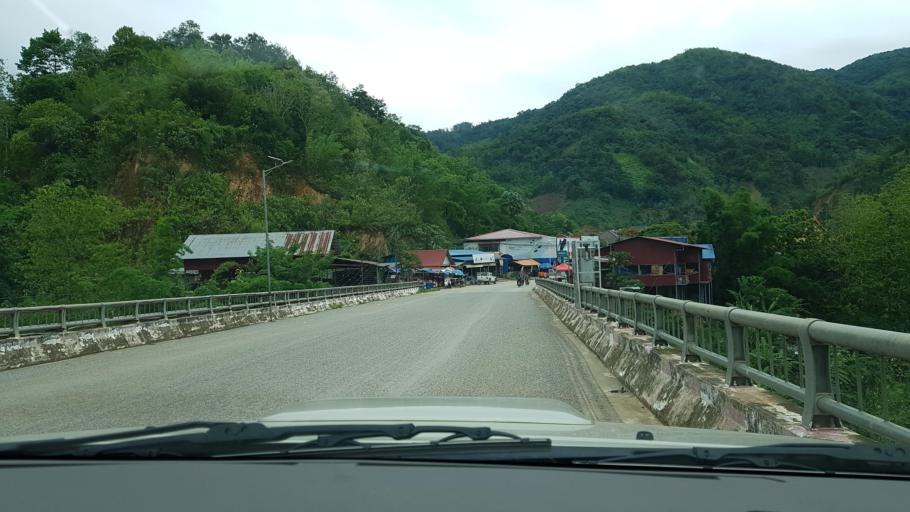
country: LA
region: Phongsali
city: Khoa
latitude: 21.0801
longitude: 102.5070
